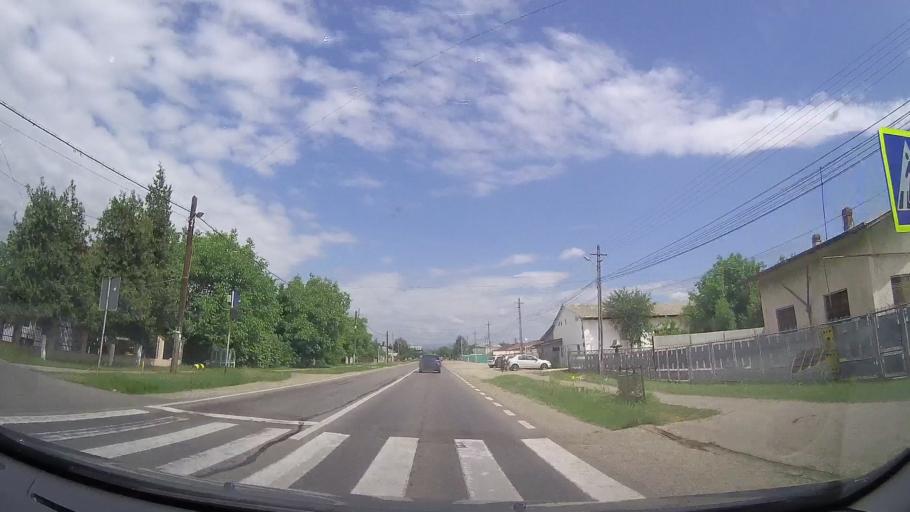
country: RO
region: Prahova
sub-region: Comuna Magurele
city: Magurele
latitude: 45.1005
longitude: 26.0361
